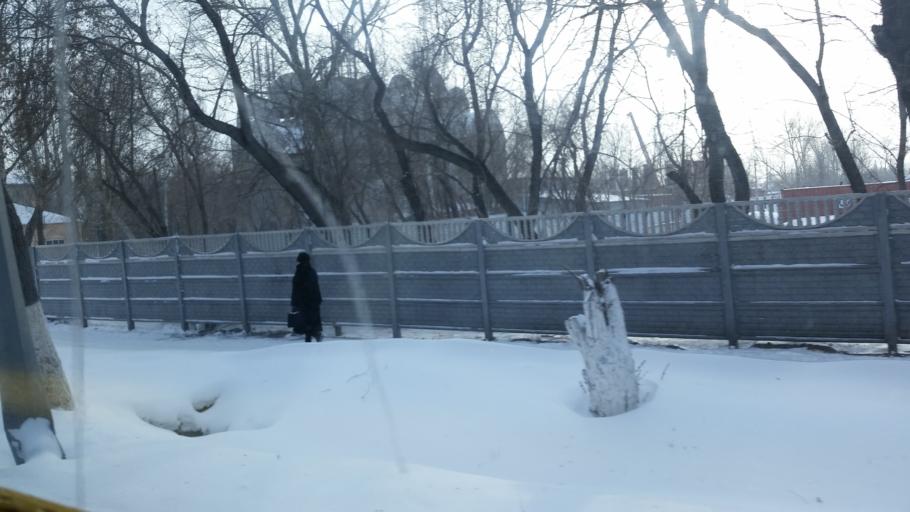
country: KZ
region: Qaraghandy
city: Aqtas
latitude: 49.8079
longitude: 73.0548
